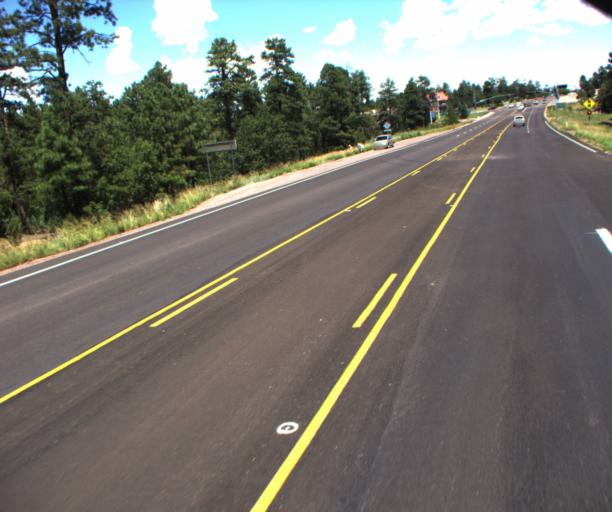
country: US
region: Arizona
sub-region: Navajo County
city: Show Low
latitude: 34.2392
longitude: -110.0609
